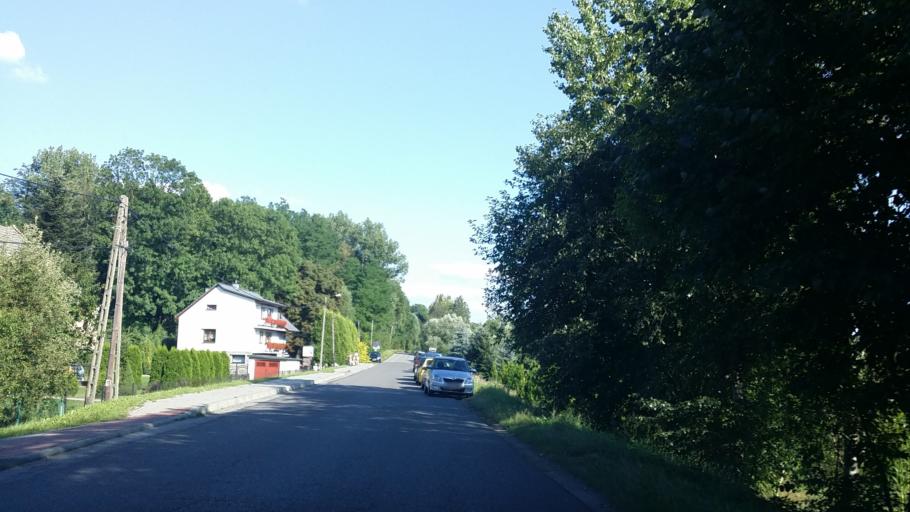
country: PL
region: Lesser Poland Voivodeship
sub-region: Powiat wadowicki
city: Wozniki
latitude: 49.9323
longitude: 19.4860
